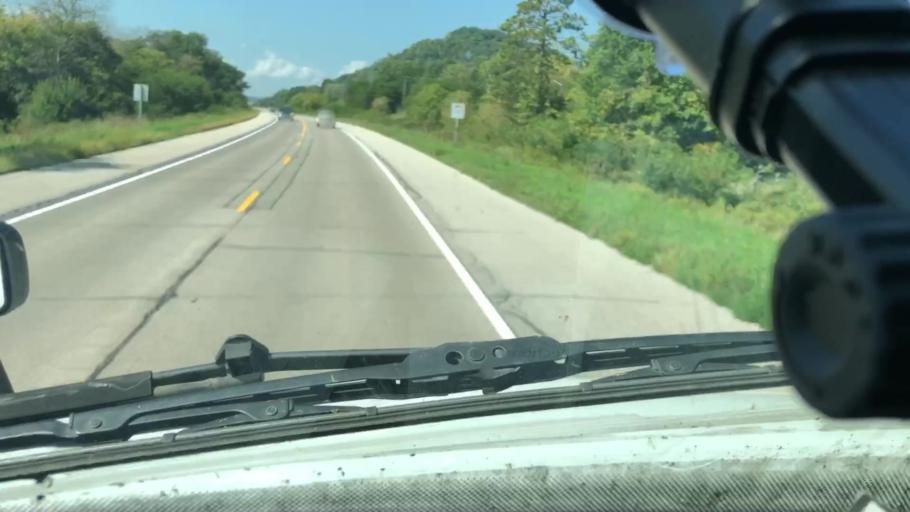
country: US
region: Minnesota
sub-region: Winona County
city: Winona
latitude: 44.0699
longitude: -91.6029
